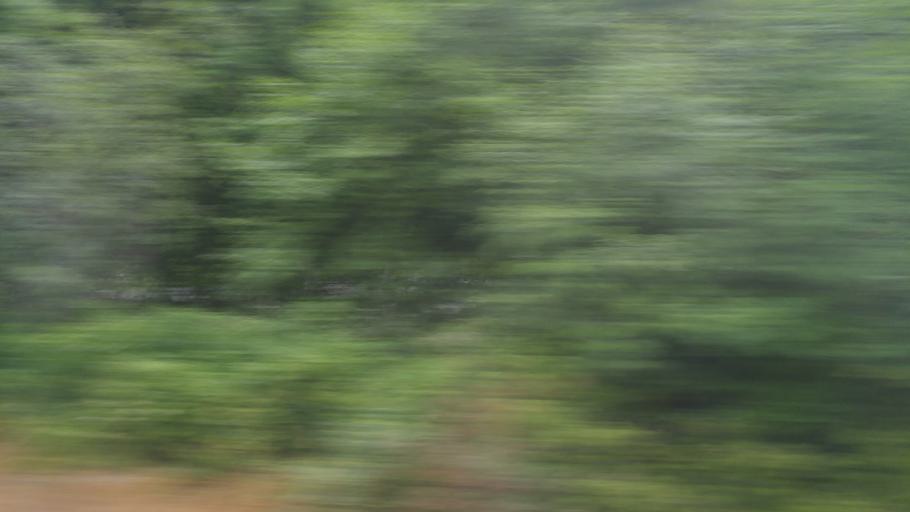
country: NO
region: Nord-Trondelag
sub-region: Stjordal
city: Stjordalshalsen
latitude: 63.4467
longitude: 10.9856
